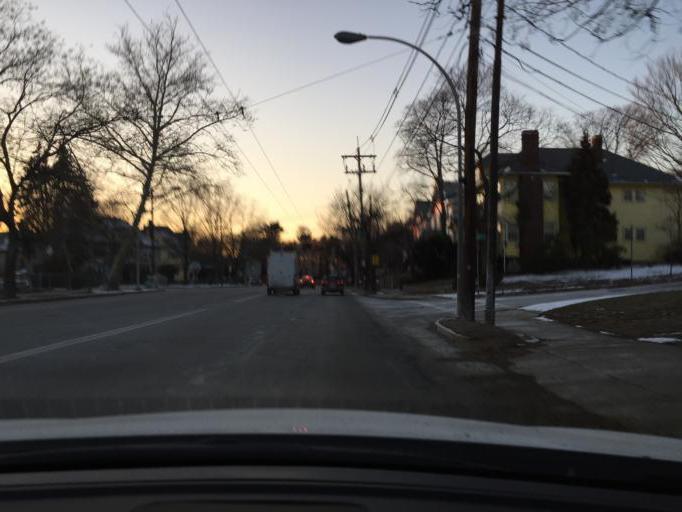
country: US
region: Massachusetts
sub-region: Middlesex County
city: Watertown
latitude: 42.3701
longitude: -71.1695
